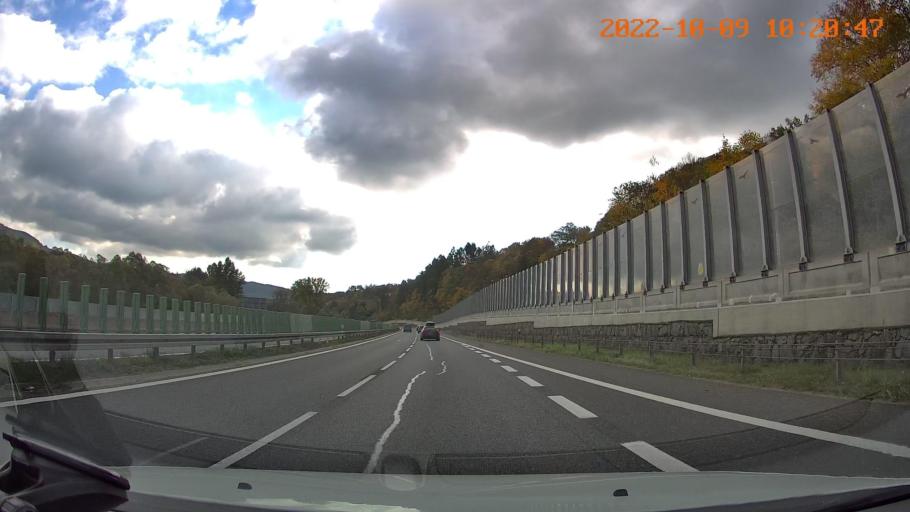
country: PL
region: Lesser Poland Voivodeship
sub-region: Powiat myslenicki
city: Stroza
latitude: 49.7916
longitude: 19.9259
